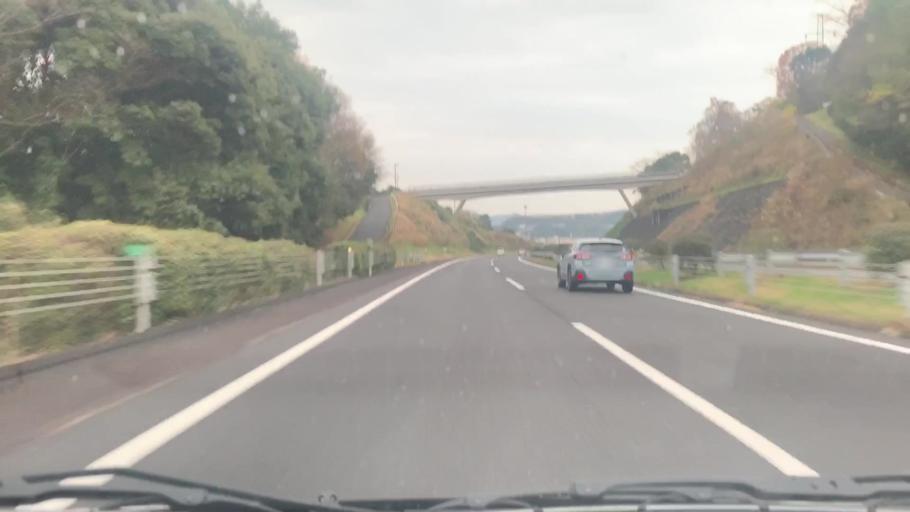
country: JP
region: Nagasaki
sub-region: Isahaya-shi
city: Isahaya
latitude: 32.8580
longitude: 130.0058
